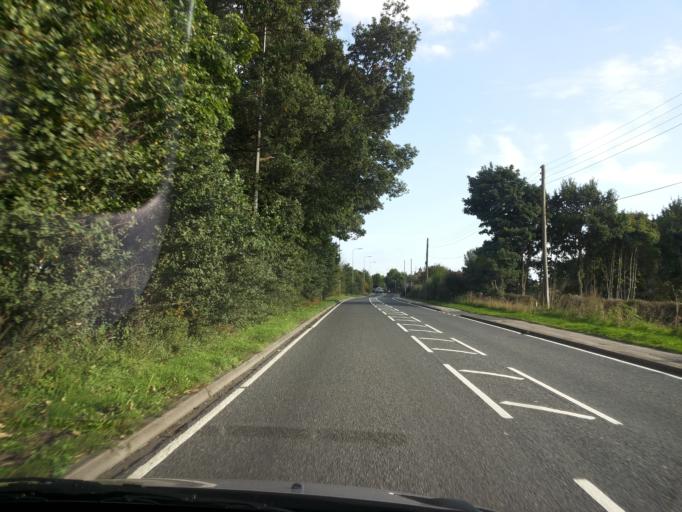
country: GB
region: England
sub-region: North Yorkshire
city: Camblesforth
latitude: 53.7293
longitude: -1.0336
